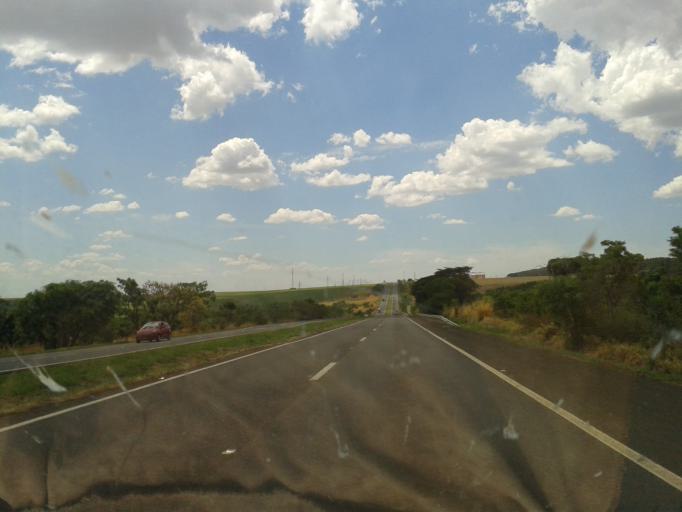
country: BR
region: Minas Gerais
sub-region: Uberlandia
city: Uberlandia
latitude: -19.0945
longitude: -48.1831
